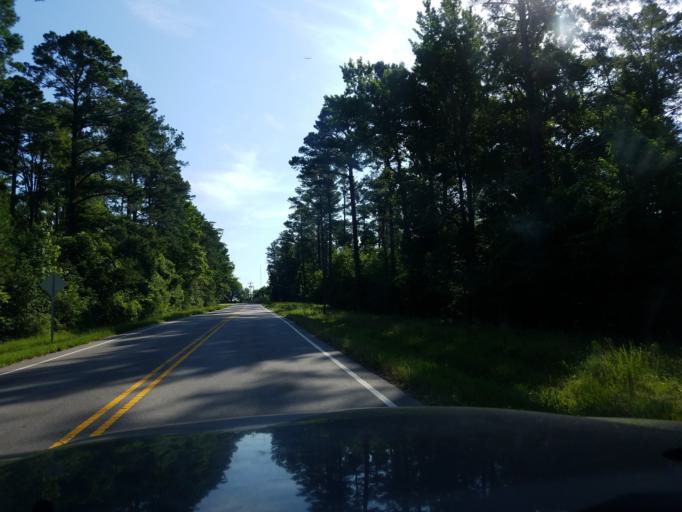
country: US
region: North Carolina
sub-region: Granville County
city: Butner
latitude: 36.1601
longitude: -78.7637
